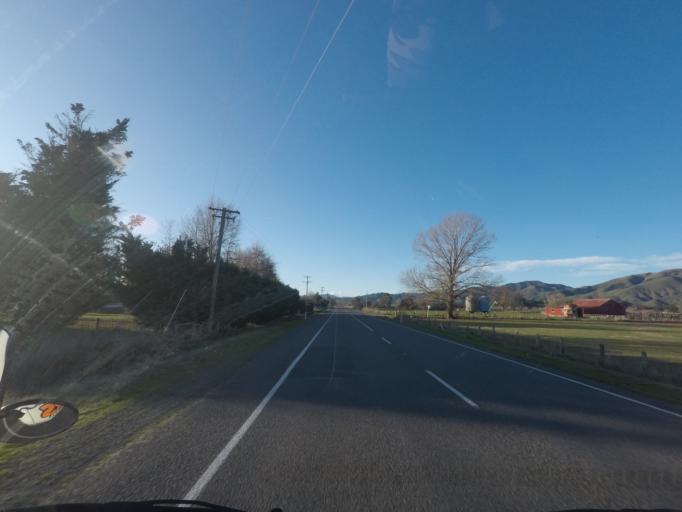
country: NZ
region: Canterbury
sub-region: Kaikoura District
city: Kaikoura
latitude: -42.7165
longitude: 173.2883
